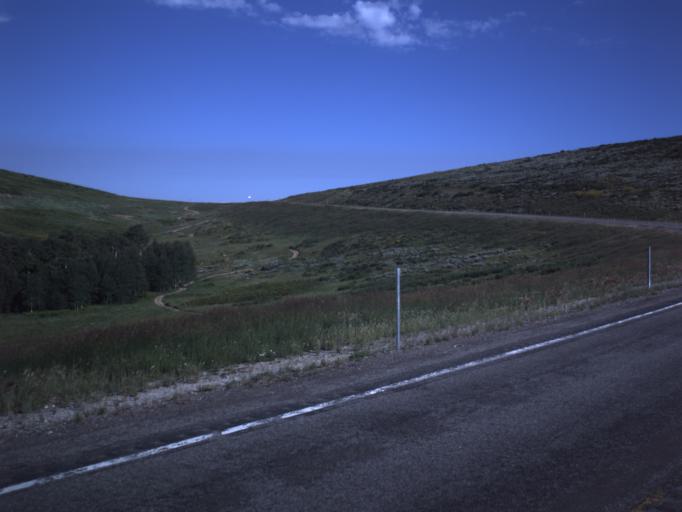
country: US
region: Utah
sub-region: Sanpete County
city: Fairview
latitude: 39.6163
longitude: -111.2811
